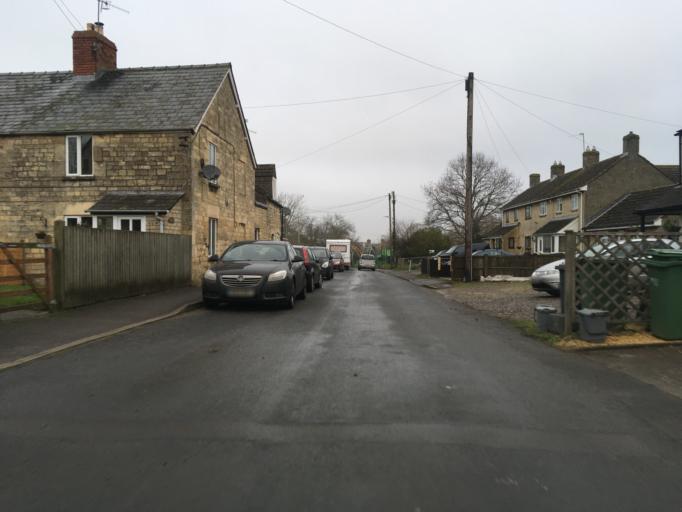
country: GB
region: England
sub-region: Gloucestershire
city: Stonehouse
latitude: 51.7293
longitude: -2.2870
